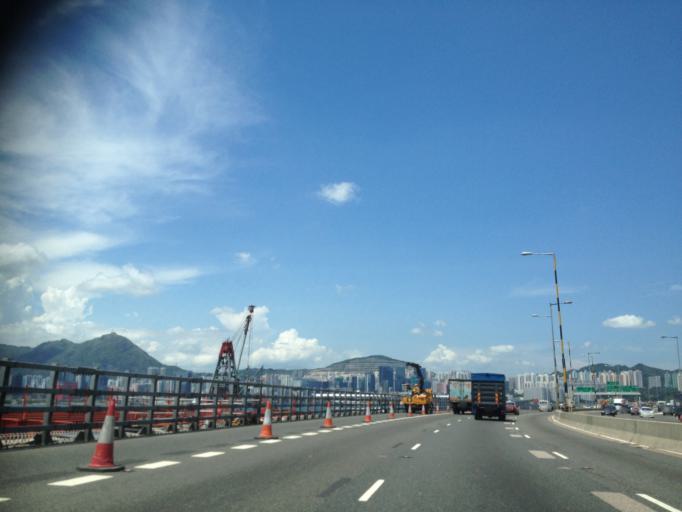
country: HK
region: Wanchai
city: Wan Chai
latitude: 22.2924
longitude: 114.1942
